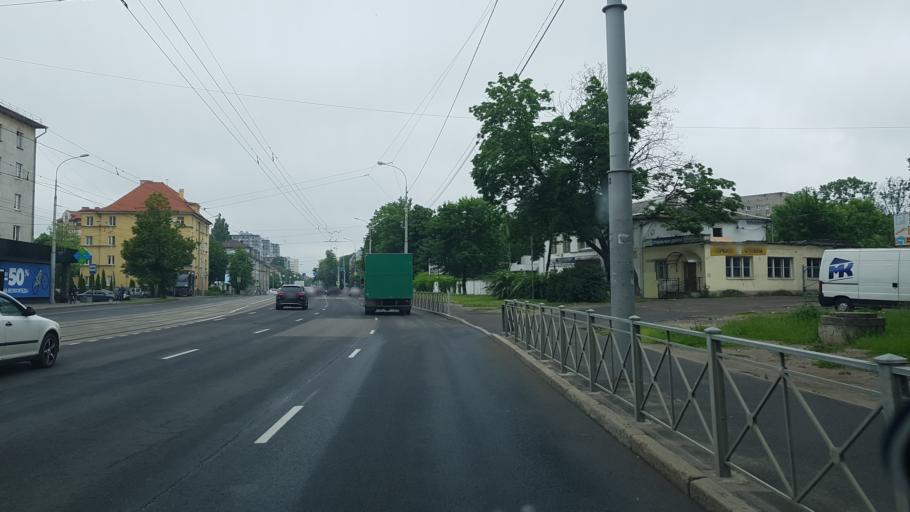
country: RU
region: Kaliningrad
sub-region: Gorod Kaliningrad
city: Kaliningrad
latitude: 54.7291
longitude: 20.4922
